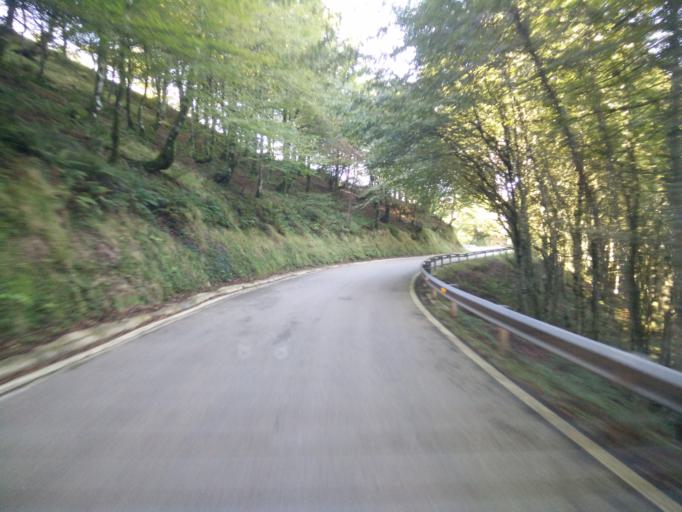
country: ES
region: Cantabria
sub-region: Provincia de Cantabria
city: San Pedro del Romeral
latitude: 43.0566
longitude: -3.8408
